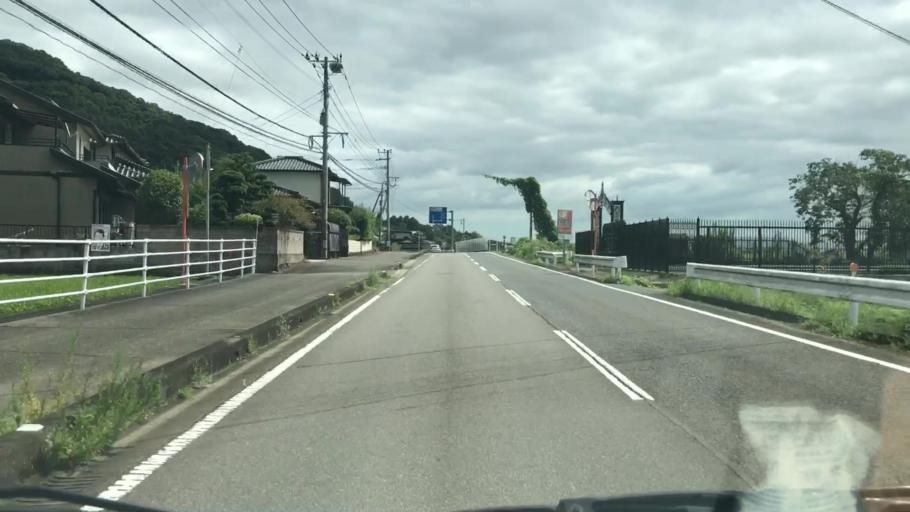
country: JP
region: Saga Prefecture
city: Kashima
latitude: 33.2272
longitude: 130.1539
